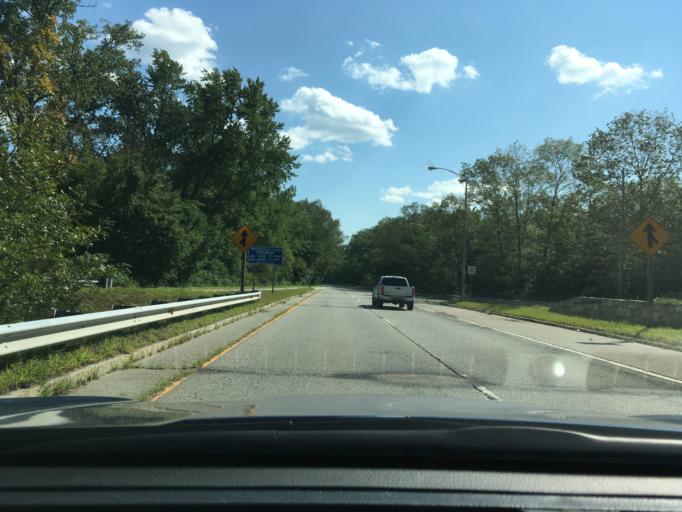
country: US
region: Rhode Island
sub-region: Kent County
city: West Warwick
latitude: 41.7351
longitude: -71.4810
